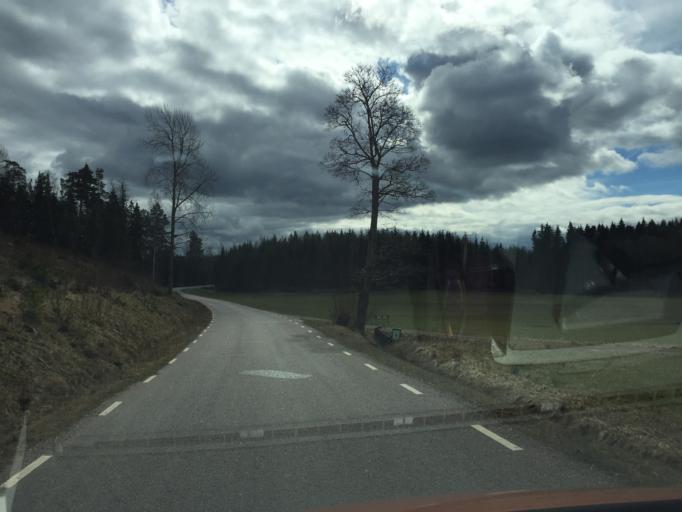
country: SE
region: Soedermanland
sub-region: Nykopings Kommun
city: Stigtomta
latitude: 58.9641
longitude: 16.8999
